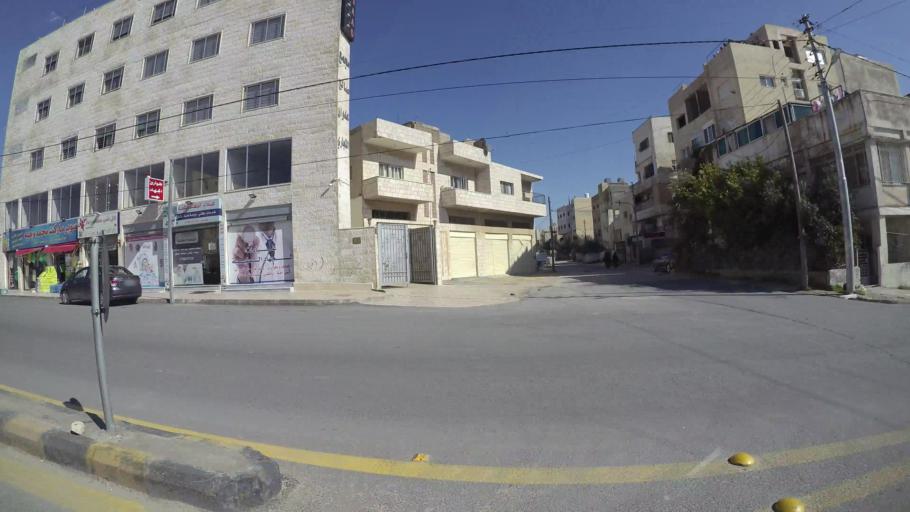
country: JO
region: Amman
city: Al Bunayyat ash Shamaliyah
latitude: 31.9071
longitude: 35.9035
